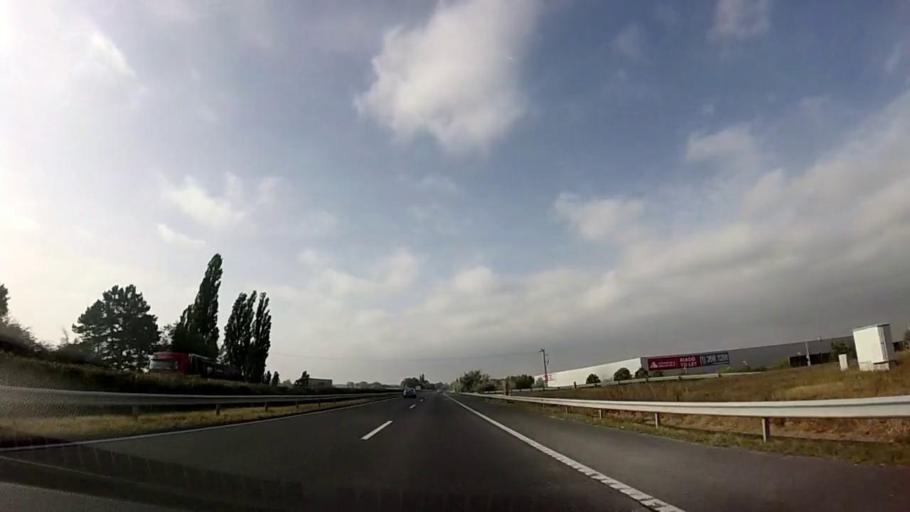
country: HU
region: Fejer
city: Szekesfehervar
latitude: 47.1474
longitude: 18.4348
